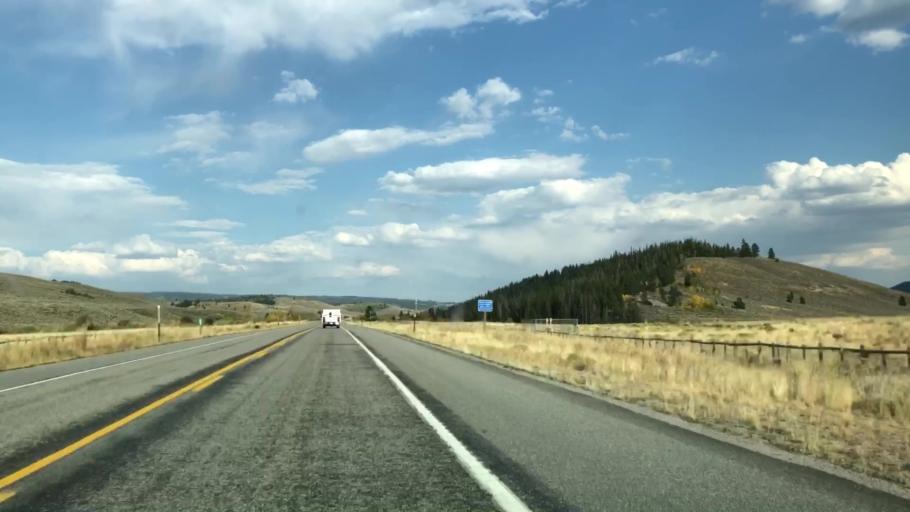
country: US
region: Wyoming
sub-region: Teton County
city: Hoback
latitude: 43.1547
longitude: -110.3294
